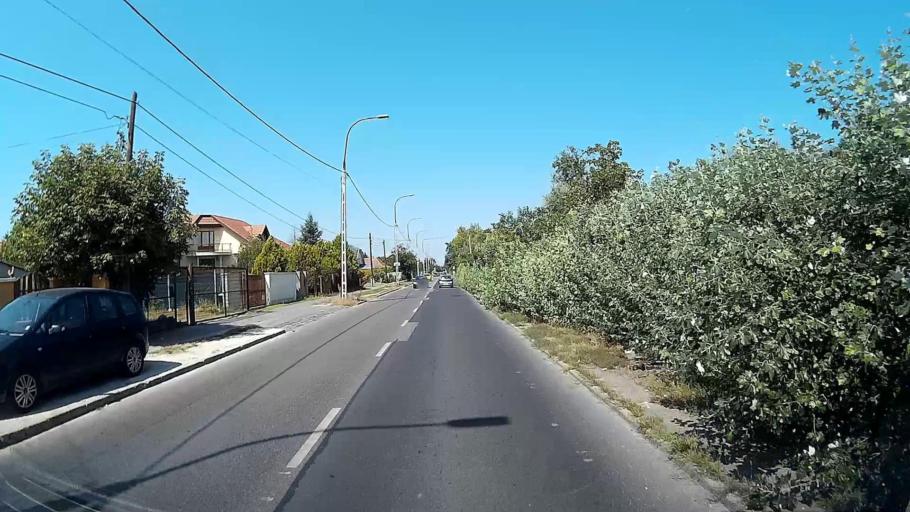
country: HU
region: Budapest
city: Budapest XXIII. keruelet
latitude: 47.4191
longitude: 19.1379
